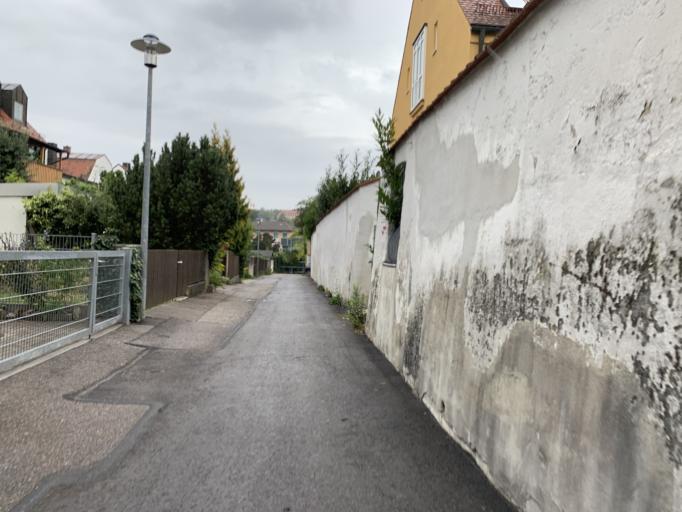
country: DE
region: Bavaria
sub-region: Upper Bavaria
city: Freising
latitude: 48.4003
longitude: 11.7394
